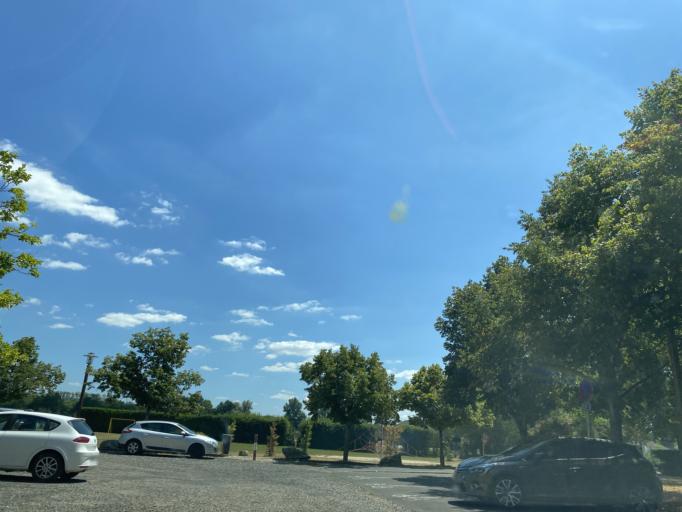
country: FR
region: Auvergne
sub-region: Departement du Puy-de-Dome
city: Peschadoires
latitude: 45.8701
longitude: 3.4824
